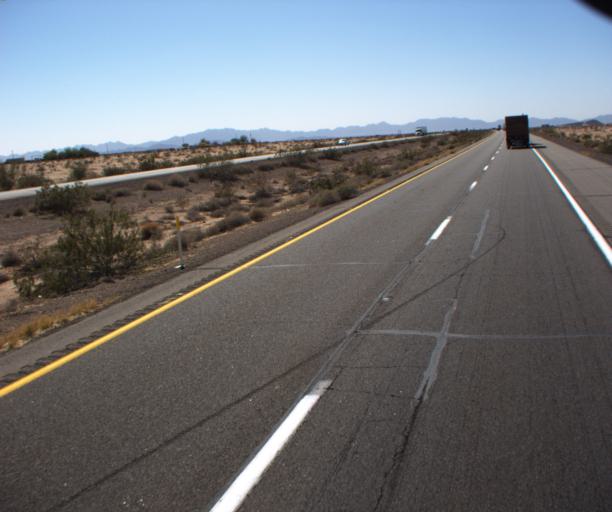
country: US
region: Arizona
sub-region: Yuma County
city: Wellton
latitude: 32.6876
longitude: -113.9933
